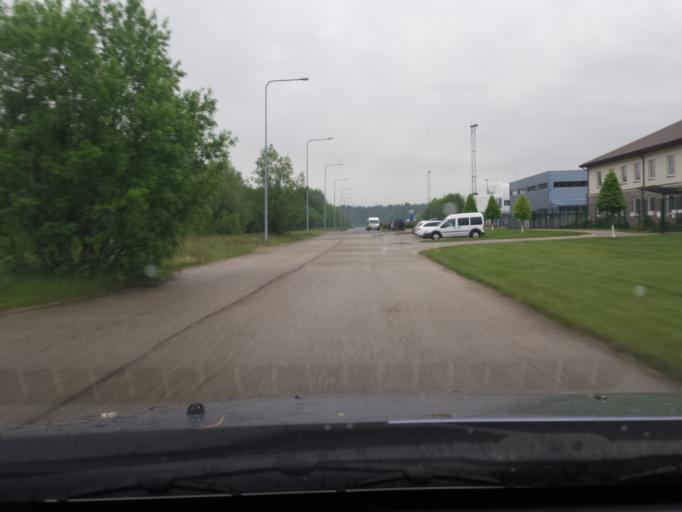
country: LV
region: Riga
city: Bolderaja
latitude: 57.0481
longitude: 24.0840
